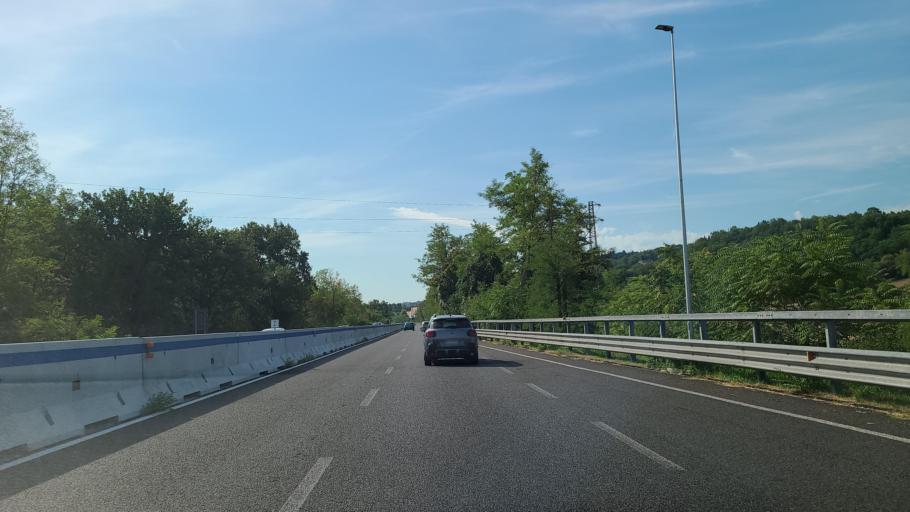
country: IT
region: Tuscany
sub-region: Province of Florence
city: Sambuca
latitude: 43.6030
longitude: 11.1921
